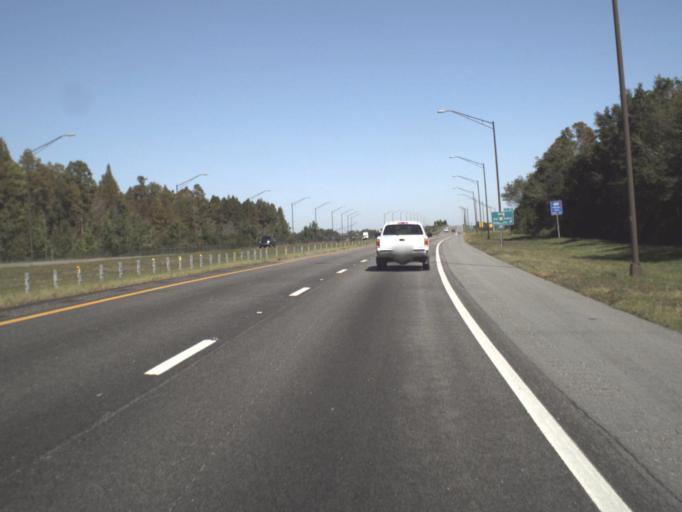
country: US
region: Florida
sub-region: Pasco County
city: Shady Hills
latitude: 28.3226
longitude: -82.5532
